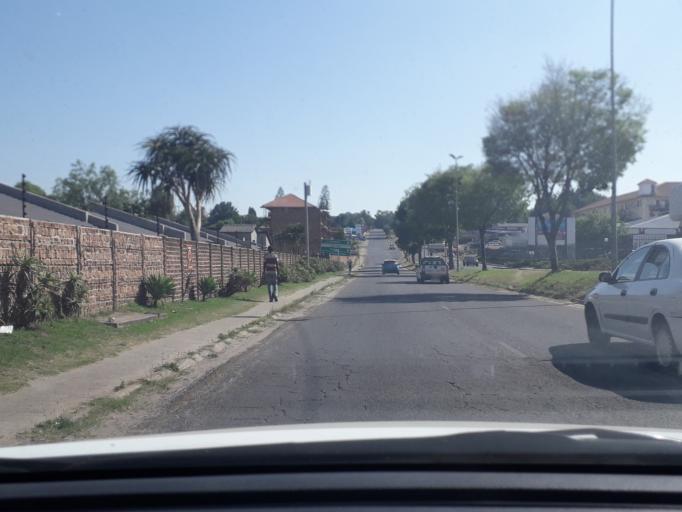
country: ZA
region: Gauteng
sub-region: City of Johannesburg Metropolitan Municipality
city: Roodepoort
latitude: -26.1064
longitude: 27.9753
